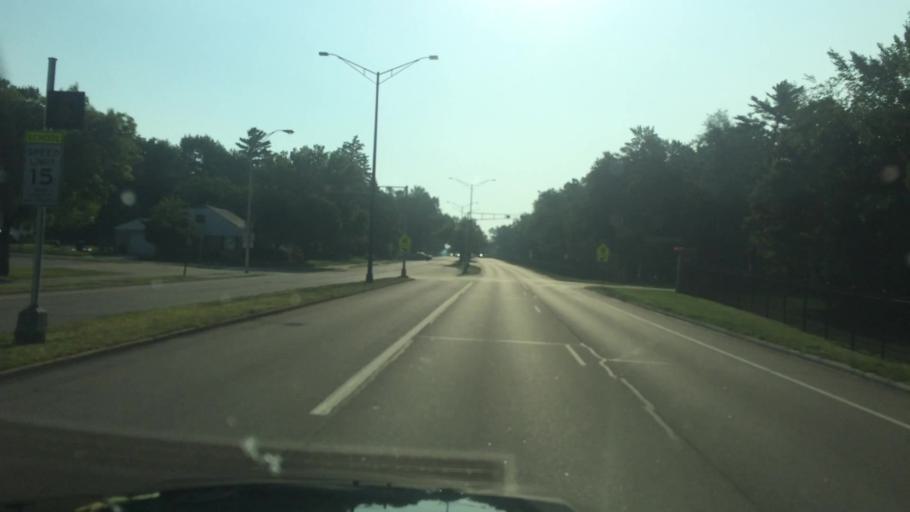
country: US
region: Wisconsin
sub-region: Marathon County
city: Wausau
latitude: 44.9591
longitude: -89.6513
